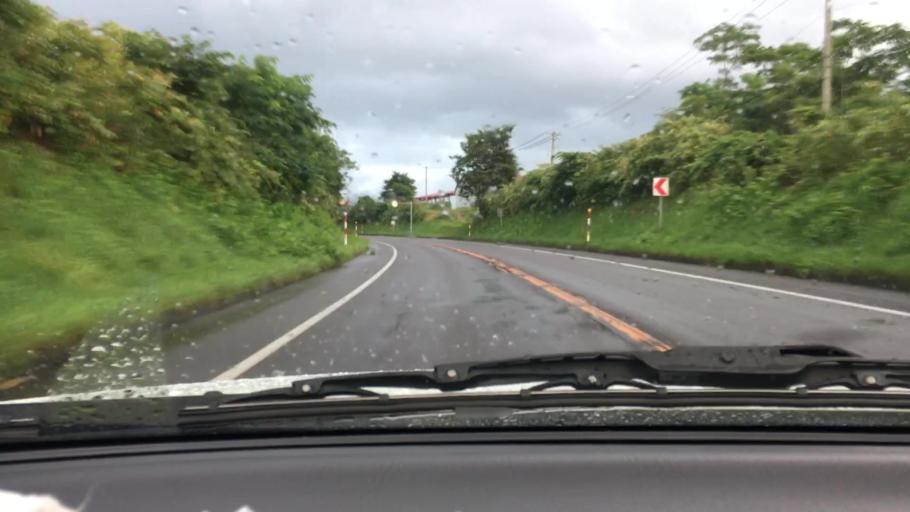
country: JP
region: Hokkaido
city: Nanae
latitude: 42.0821
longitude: 140.5876
